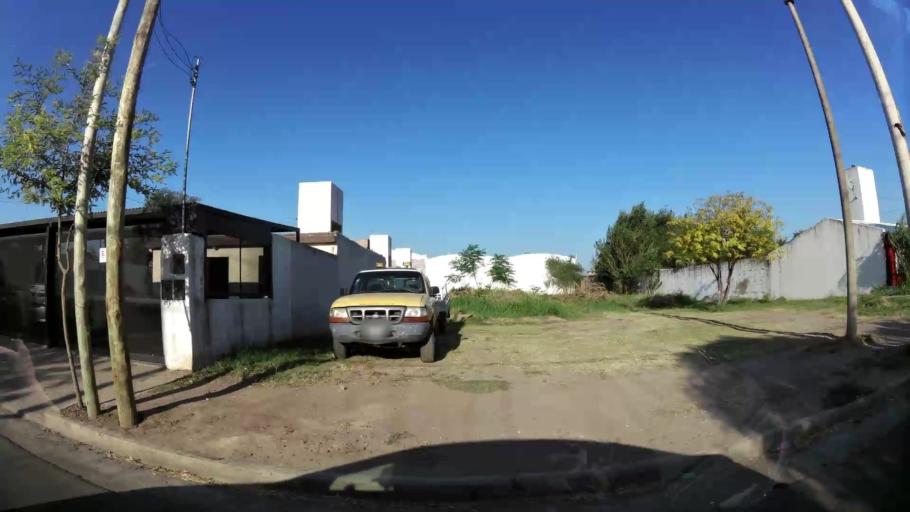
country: AR
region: Cordoba
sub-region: Departamento de Capital
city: Cordoba
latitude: -31.4427
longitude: -64.2480
